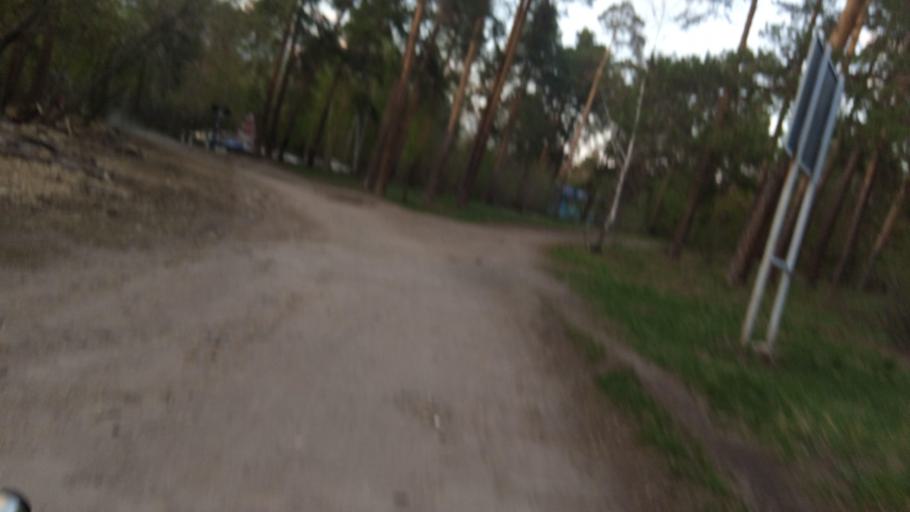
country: RU
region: Chelyabinsk
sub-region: Gorod Chelyabinsk
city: Chelyabinsk
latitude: 55.1663
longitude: 61.3407
